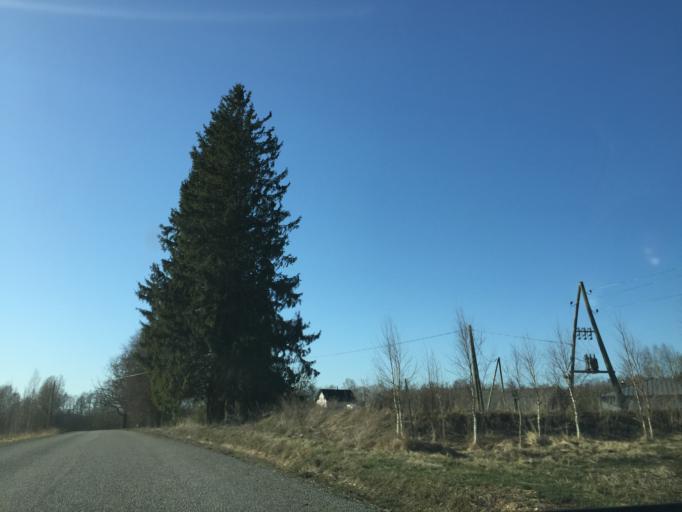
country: LV
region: Malpils
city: Malpils
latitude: 57.1023
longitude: 24.9915
